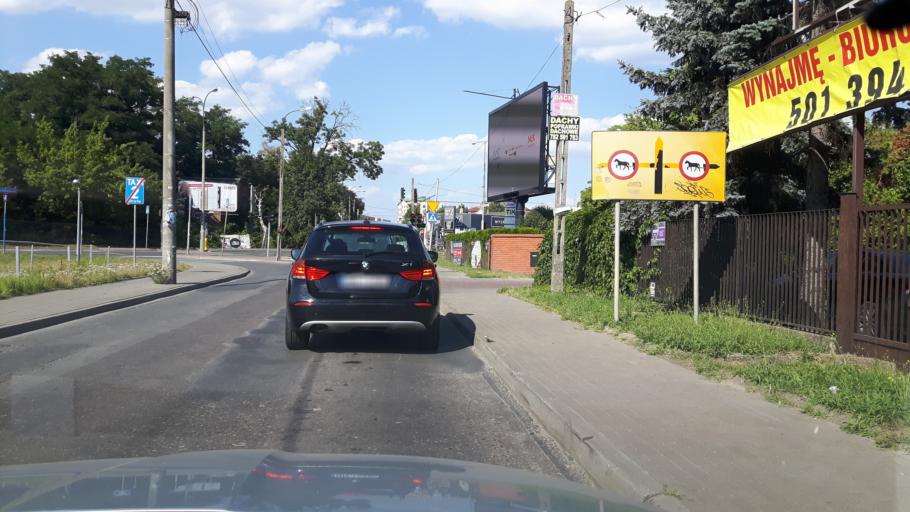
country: PL
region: Masovian Voivodeship
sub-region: Warszawa
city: Ursus
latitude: 52.1852
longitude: 20.9044
